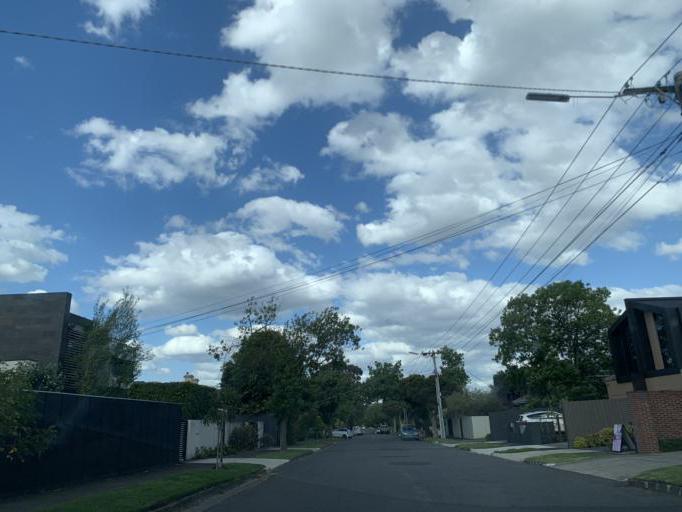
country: AU
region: Victoria
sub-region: Bayside
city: Hampton
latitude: -37.9233
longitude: 145.0056
